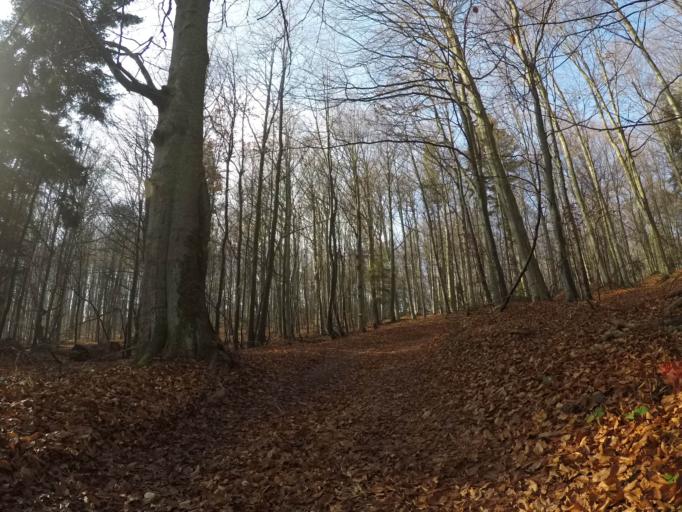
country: SK
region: Kosicky
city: Gelnica
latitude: 48.7630
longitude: 21.0747
